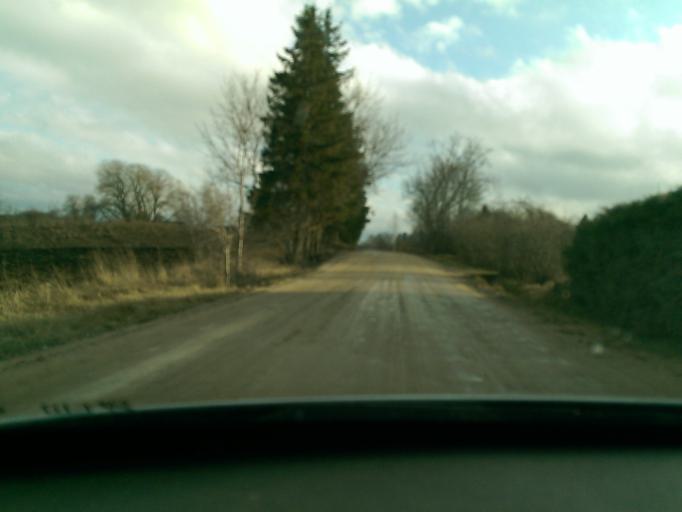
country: LV
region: Kuldigas Rajons
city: Kuldiga
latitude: 56.9738
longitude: 21.9927
